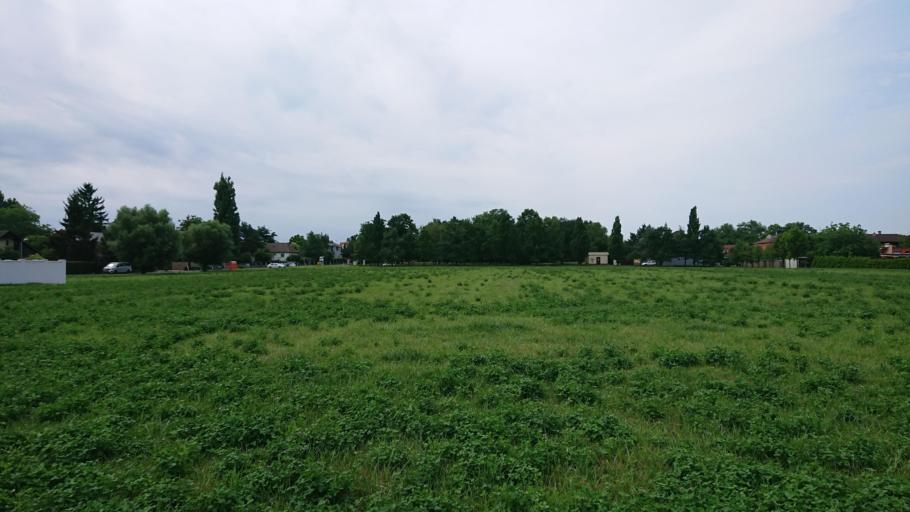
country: CZ
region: Praha
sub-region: Praha 19
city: Satalice
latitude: 50.1276
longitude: 14.5679
